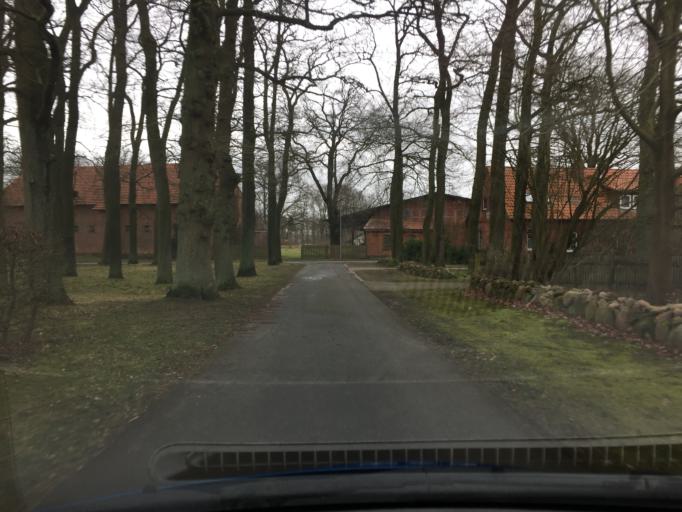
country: DE
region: Lower Saxony
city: Stoetze
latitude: 53.0547
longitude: 10.8181
